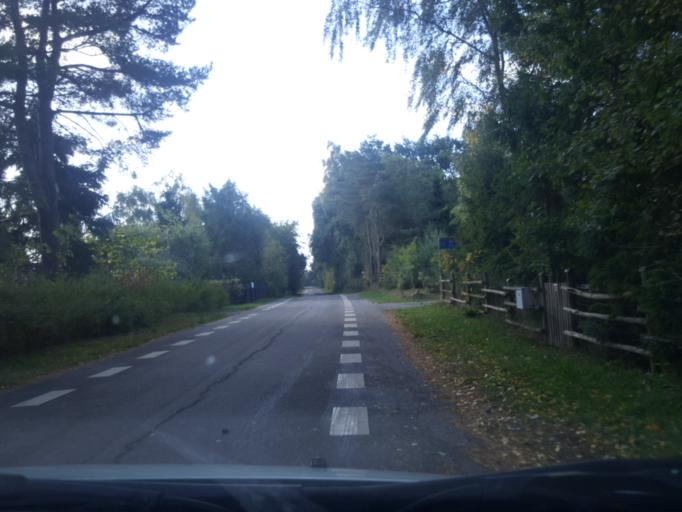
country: DK
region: Zealand
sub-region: Guldborgsund Kommune
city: Nykobing Falster
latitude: 54.6642
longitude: 11.9566
